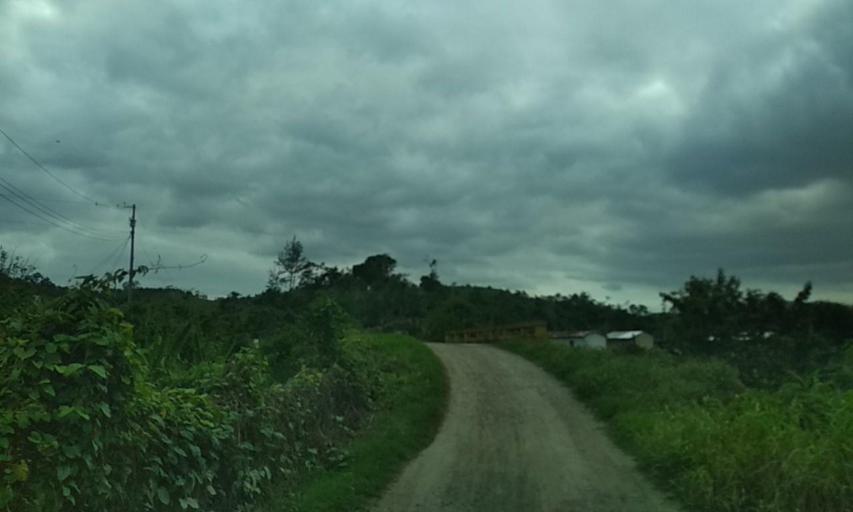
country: MX
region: Veracruz
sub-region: Papantla
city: Polutla
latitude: 20.5162
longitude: -97.2974
